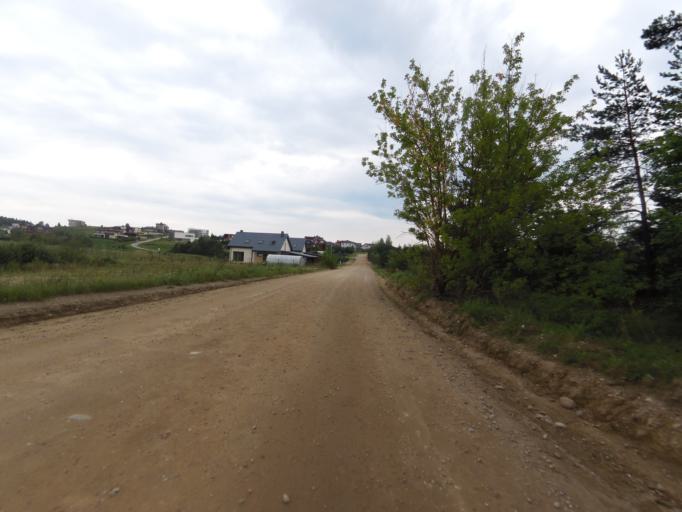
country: LT
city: Grigiskes
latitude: 54.7105
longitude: 25.1290
